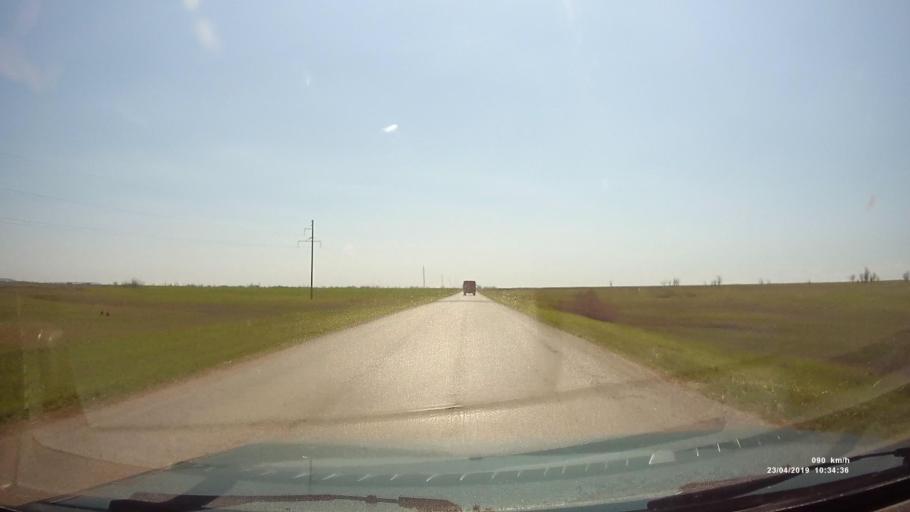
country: RU
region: Kalmykiya
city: Yashalta
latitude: 46.5630
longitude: 42.6114
